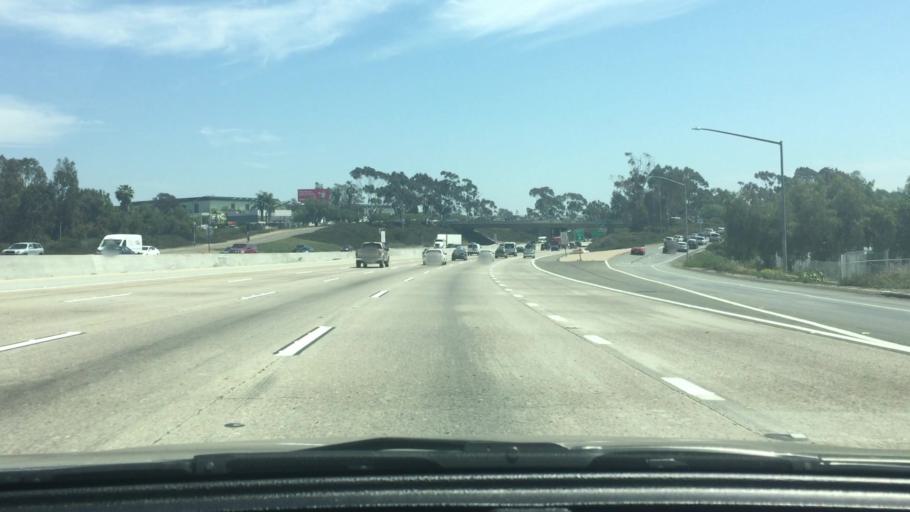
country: US
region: California
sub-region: San Diego County
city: National City
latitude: 32.7068
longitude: -117.0966
